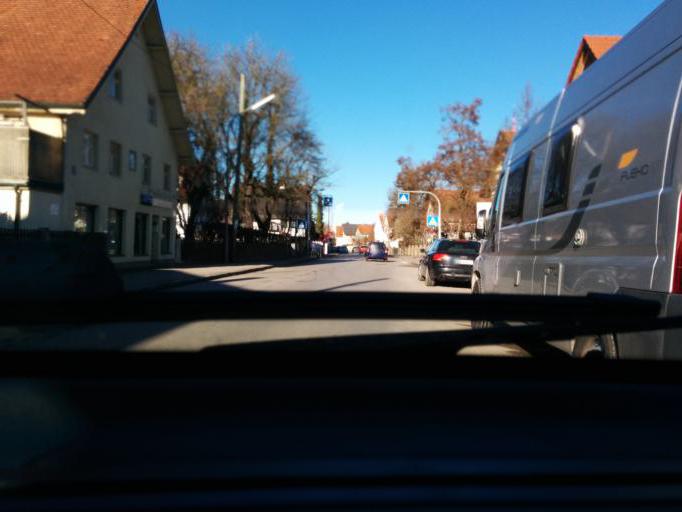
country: DE
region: Bavaria
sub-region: Upper Bavaria
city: Grafelfing
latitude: 48.1587
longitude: 11.4132
